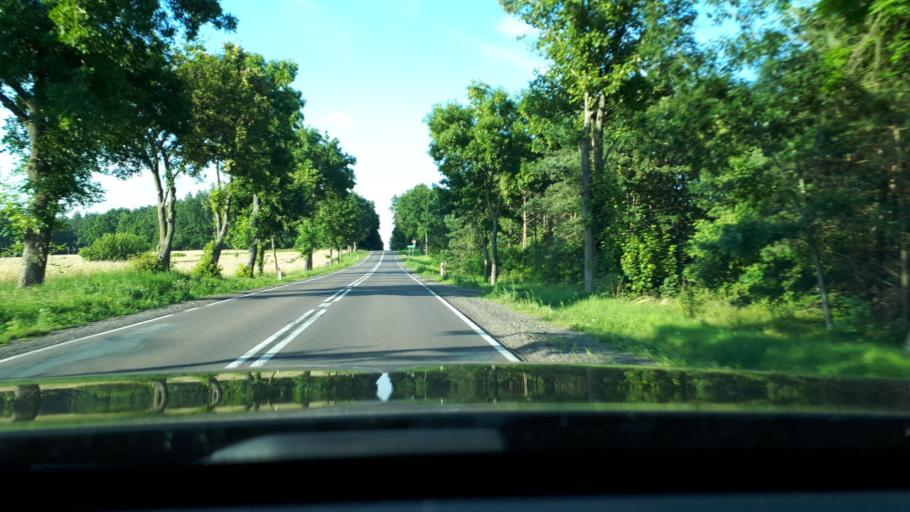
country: PL
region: Masovian Voivodeship
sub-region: Powiat ciechanowski
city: Ojrzen
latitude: 52.7794
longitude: 20.5561
